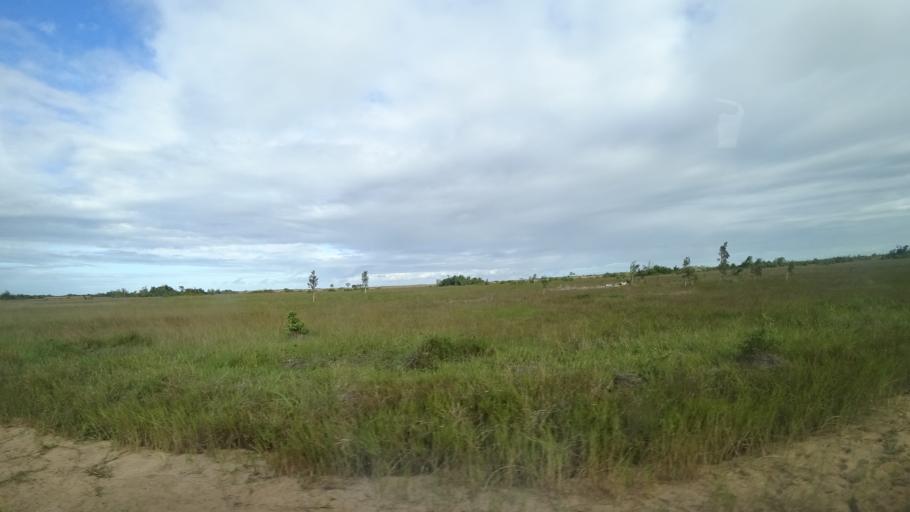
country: MZ
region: Sofala
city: Beira
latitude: -19.6873
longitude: 35.0471
